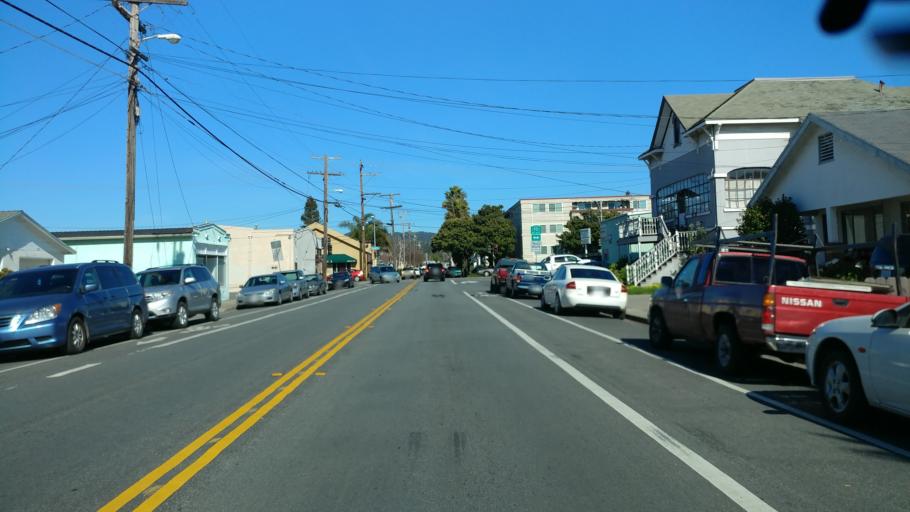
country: US
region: California
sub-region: Alameda County
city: San Leandro
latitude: 37.7200
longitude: -122.1542
